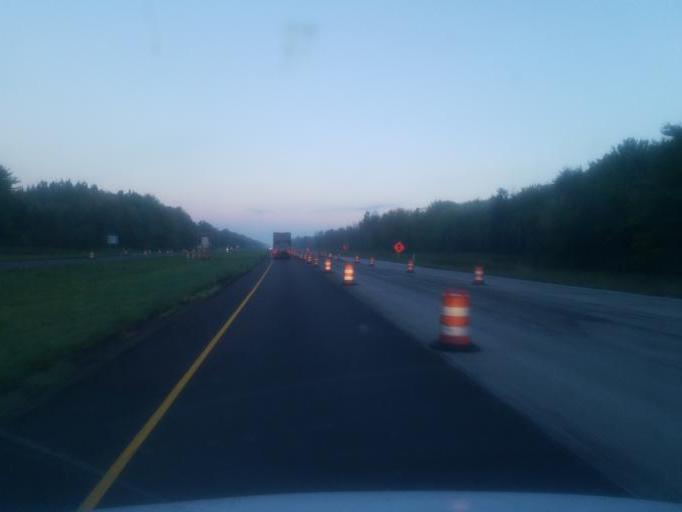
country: US
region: Ohio
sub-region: Ashtabula County
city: Jefferson
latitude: 41.7532
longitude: -80.7126
